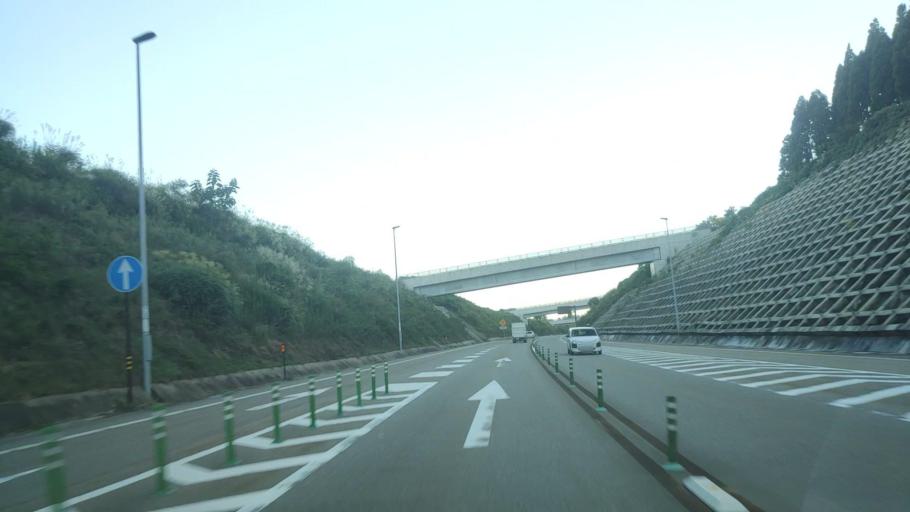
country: JP
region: Ishikawa
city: Nanao
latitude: 36.9695
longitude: 137.0489
